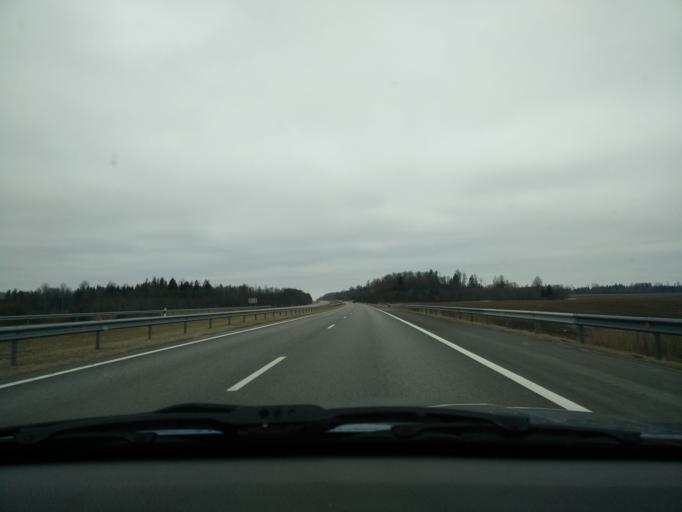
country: LT
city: Rietavas
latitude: 55.6301
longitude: 21.9608
